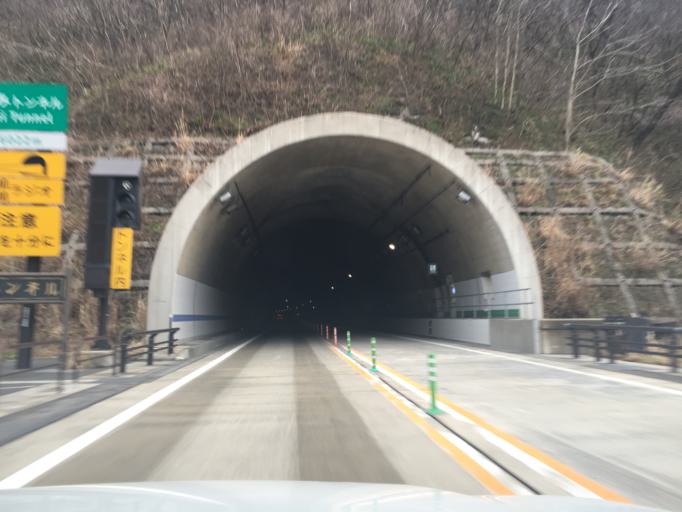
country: JP
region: Yamagata
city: Tsuruoka
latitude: 38.6174
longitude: 139.5943
